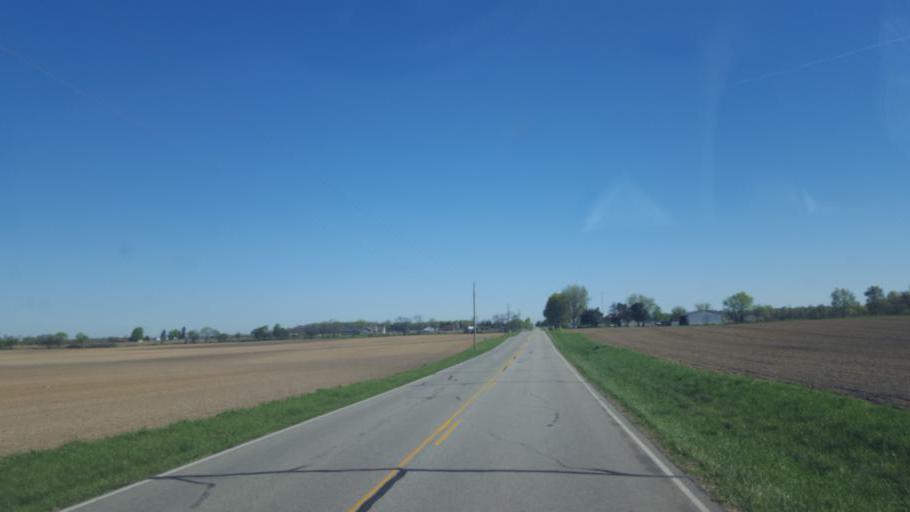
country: US
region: Ohio
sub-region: Crawford County
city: Bucyrus
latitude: 40.7508
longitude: -83.0925
